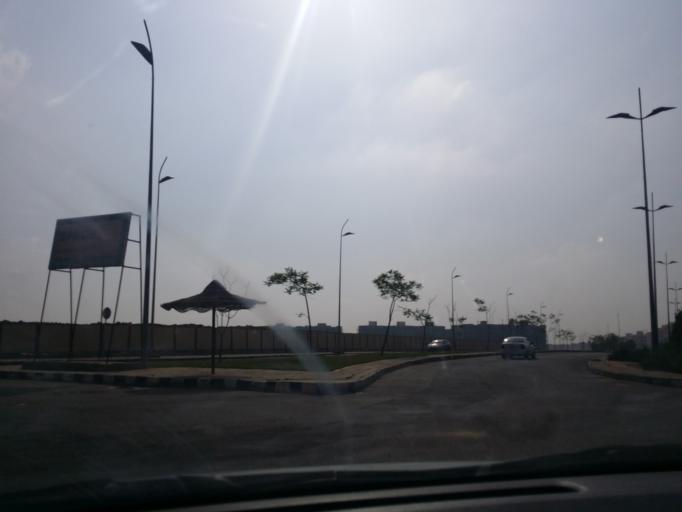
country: EG
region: Muhafazat al Qalyubiyah
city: Al Khankah
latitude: 30.0819
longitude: 31.6499
